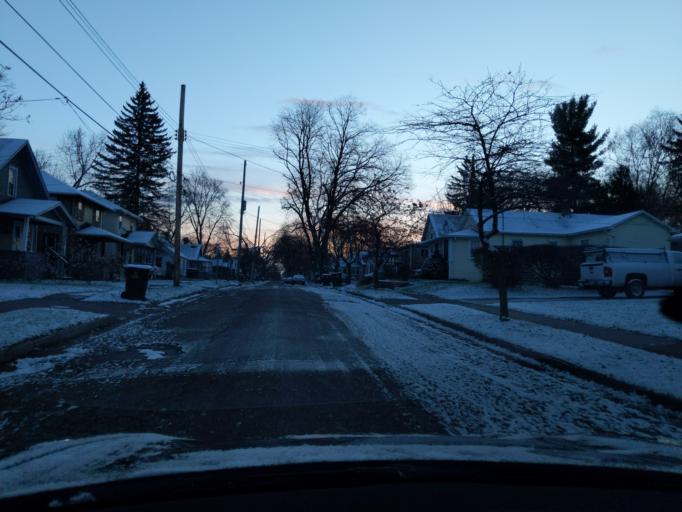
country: US
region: Michigan
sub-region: Ingham County
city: Lansing
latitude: 42.7028
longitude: -84.5520
